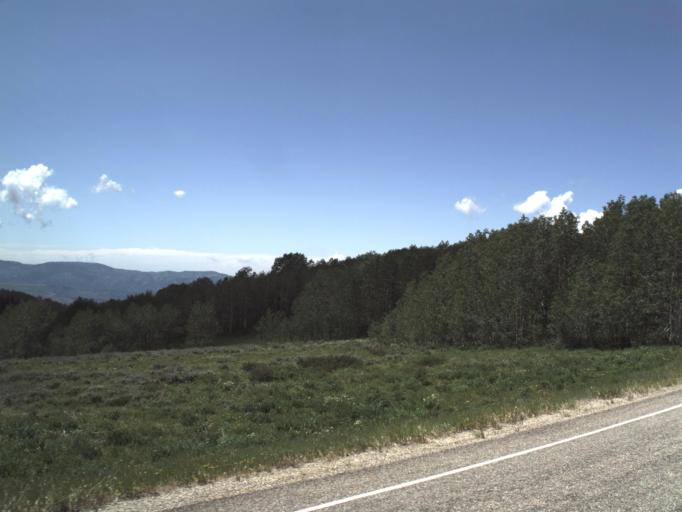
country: US
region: Utah
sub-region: Weber County
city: Wolf Creek
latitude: 41.4368
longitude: -111.5026
